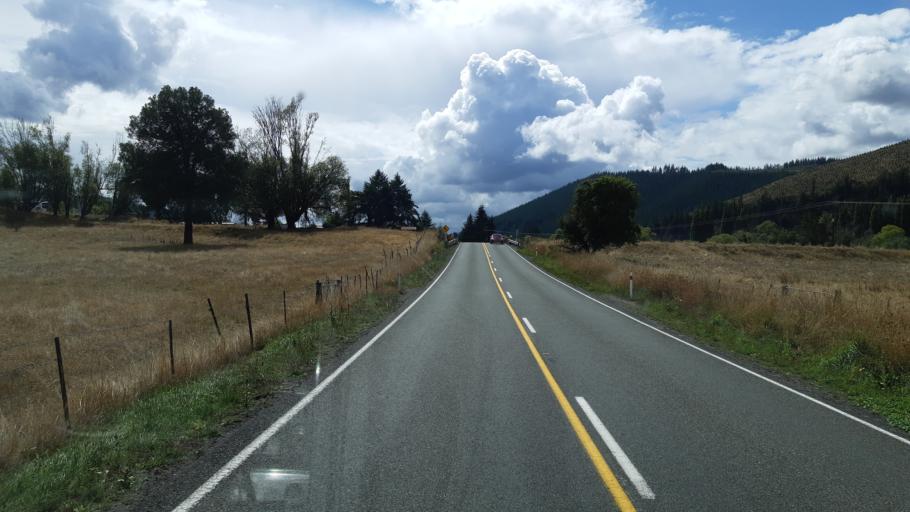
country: NZ
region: Tasman
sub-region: Tasman District
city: Wakefield
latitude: -41.4819
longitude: 172.8002
